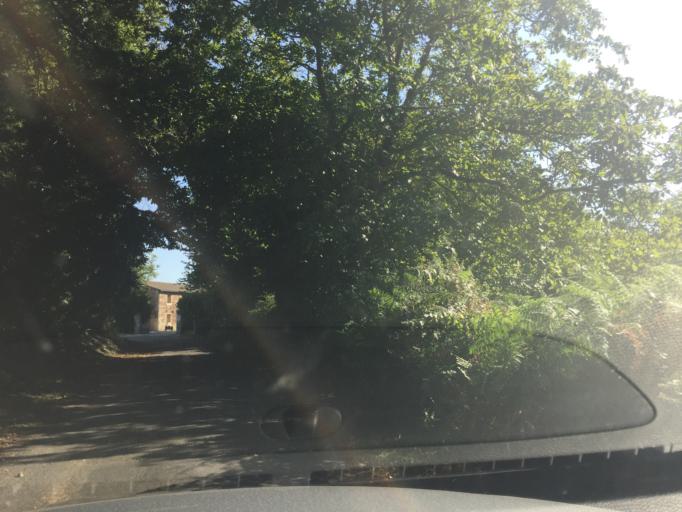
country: FR
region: Poitou-Charentes
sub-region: Departement des Deux-Sevres
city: Lezay
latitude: 46.2003
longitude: -0.0367
